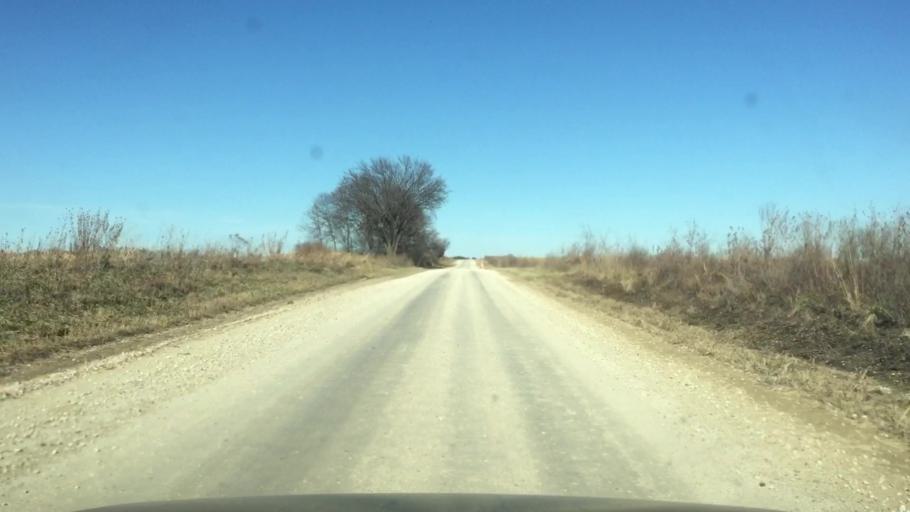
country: US
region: Kansas
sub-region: Allen County
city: Humboldt
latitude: 37.8564
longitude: -95.3910
